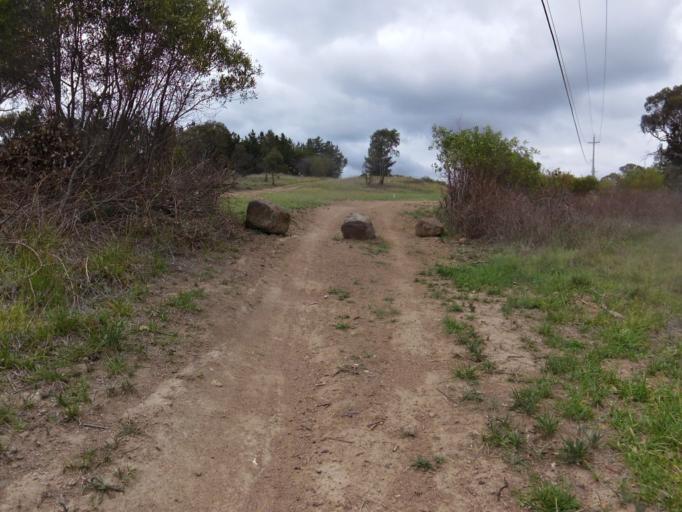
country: AU
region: Australian Capital Territory
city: Macquarie
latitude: -35.3292
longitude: 149.0260
